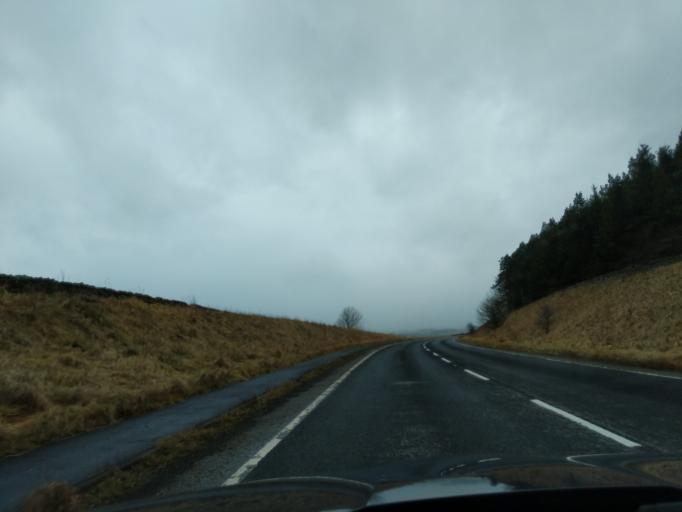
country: GB
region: England
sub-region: Northumberland
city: Otterburn
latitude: 55.2178
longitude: -2.1283
